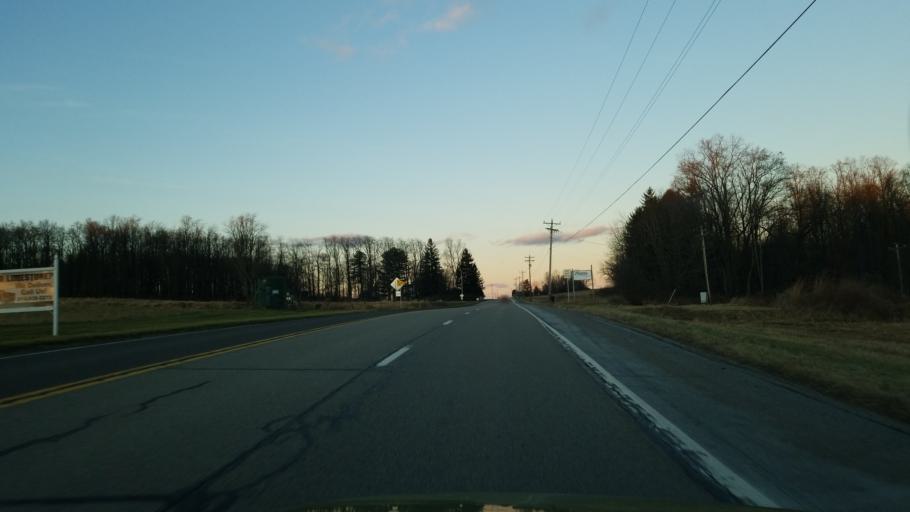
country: US
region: Pennsylvania
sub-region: Jefferson County
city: Punxsutawney
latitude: 40.8405
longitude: -79.0423
